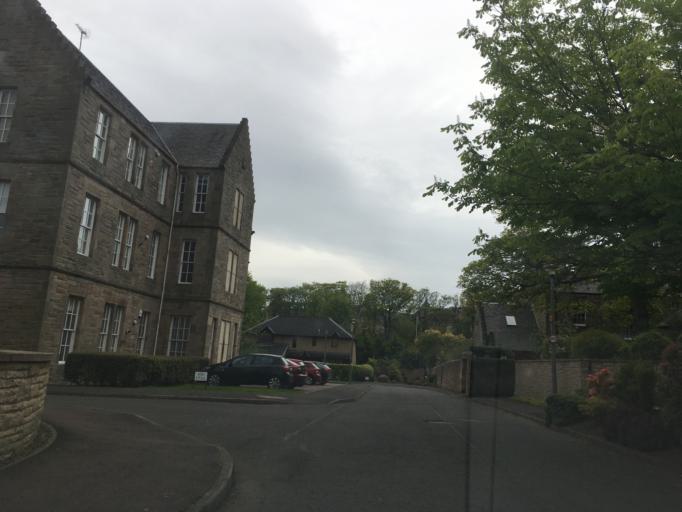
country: GB
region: Scotland
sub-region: Edinburgh
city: Colinton
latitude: 55.9177
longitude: -3.2272
